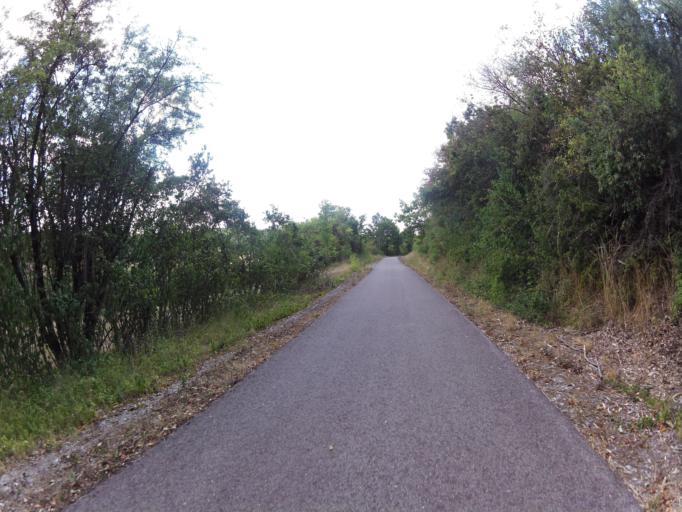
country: DE
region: Bavaria
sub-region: Regierungsbezirk Unterfranken
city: Bieberehren
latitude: 49.5207
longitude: 10.0265
